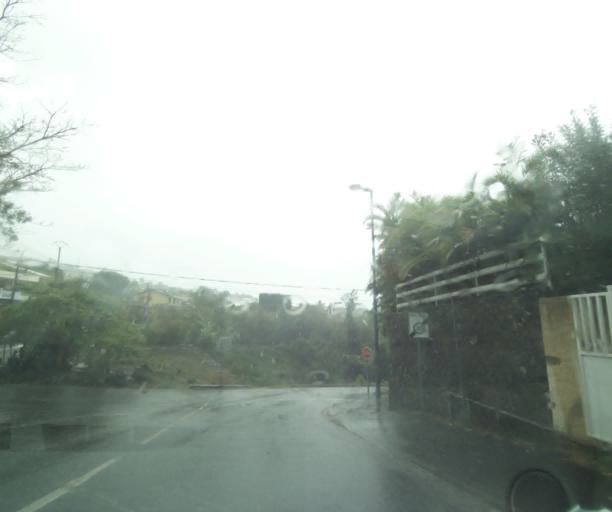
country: RE
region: Reunion
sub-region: Reunion
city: Saint-Paul
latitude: -20.9917
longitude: 55.3273
